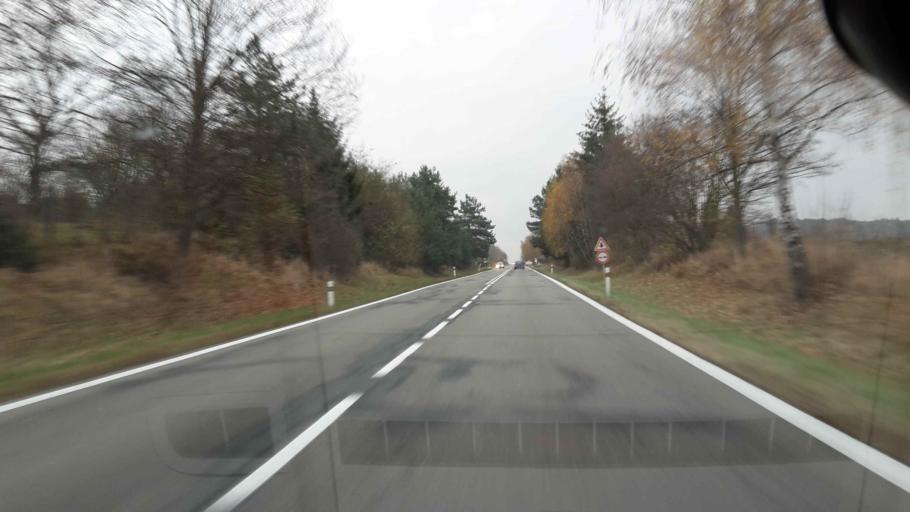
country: CZ
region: South Moravian
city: Lipuvka
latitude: 49.3339
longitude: 16.5711
